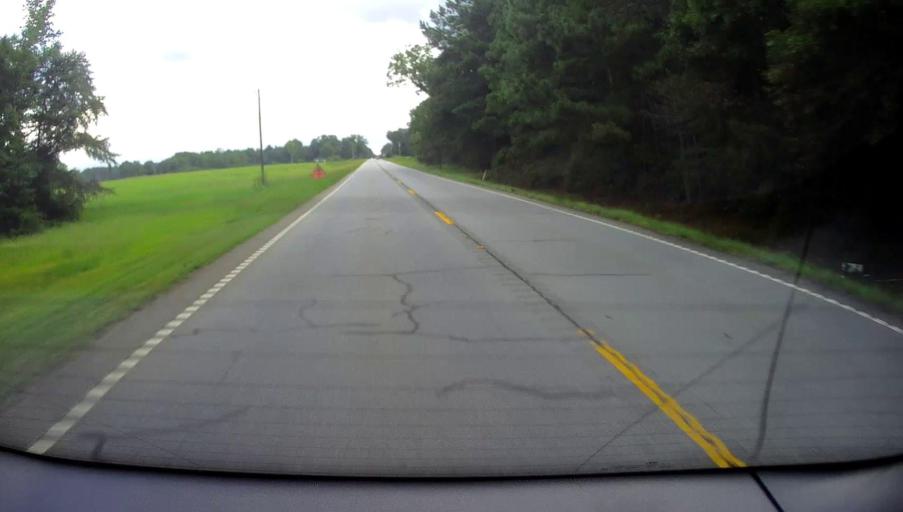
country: US
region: Georgia
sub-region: Coweta County
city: Senoia
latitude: 33.2062
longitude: -84.5804
